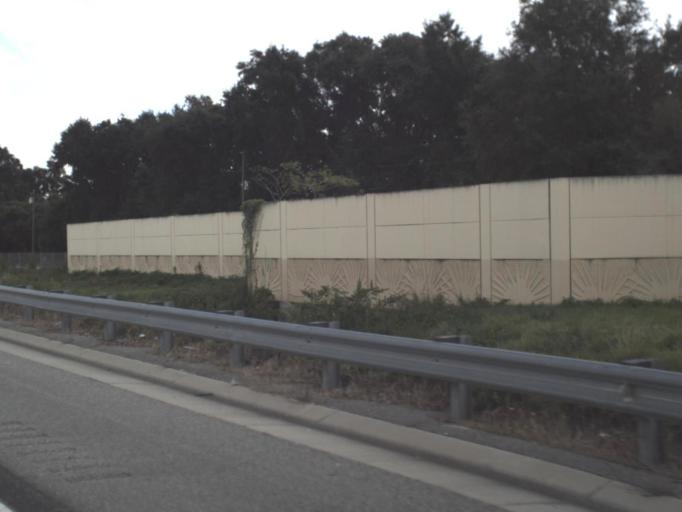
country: US
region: Florida
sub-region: Orange County
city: Winter Garden
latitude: 28.5451
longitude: -81.5752
